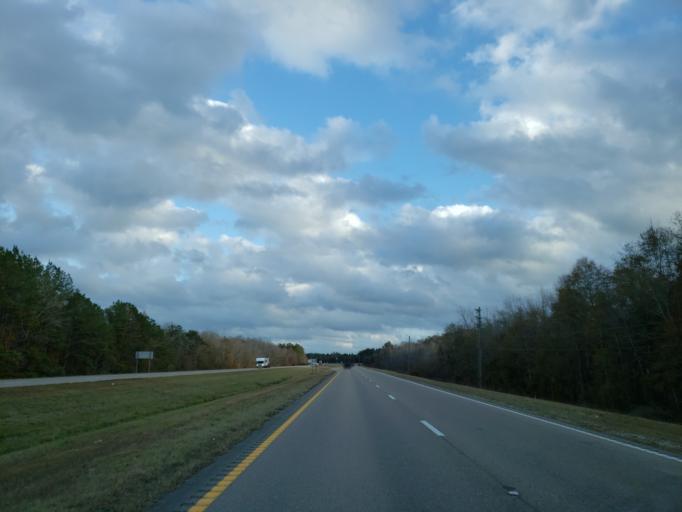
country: US
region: Mississippi
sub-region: Perry County
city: New Augusta
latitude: 31.1491
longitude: -88.8875
